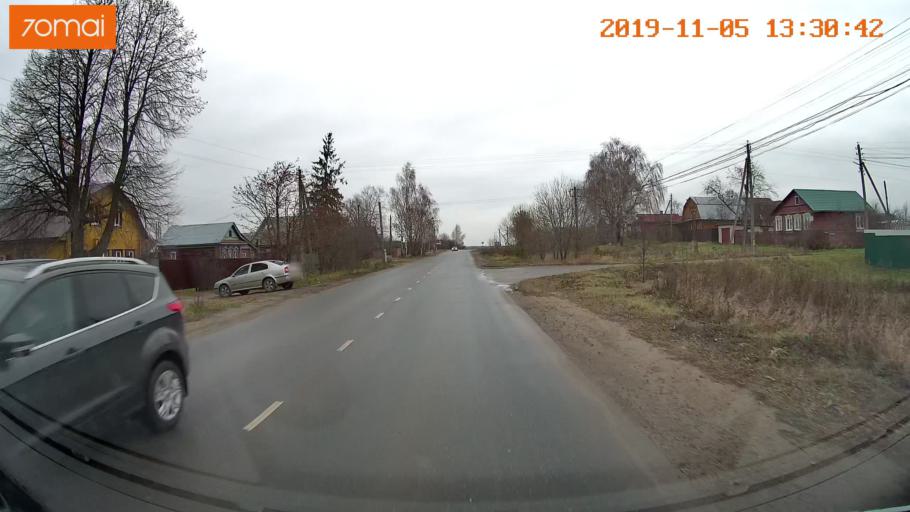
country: RU
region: Ivanovo
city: Shuya
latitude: 56.8689
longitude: 41.3946
